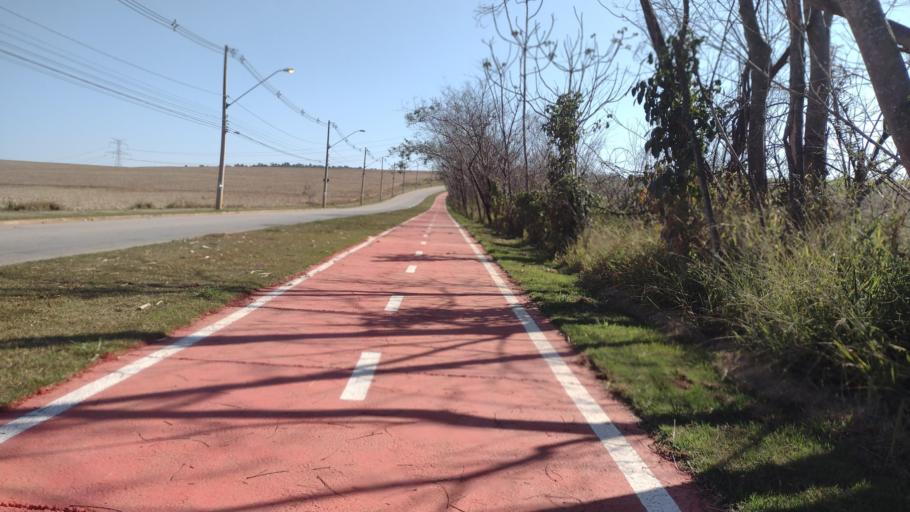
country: BR
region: Sao Paulo
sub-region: Sorocaba
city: Sorocaba
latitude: -23.4042
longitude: -47.4786
